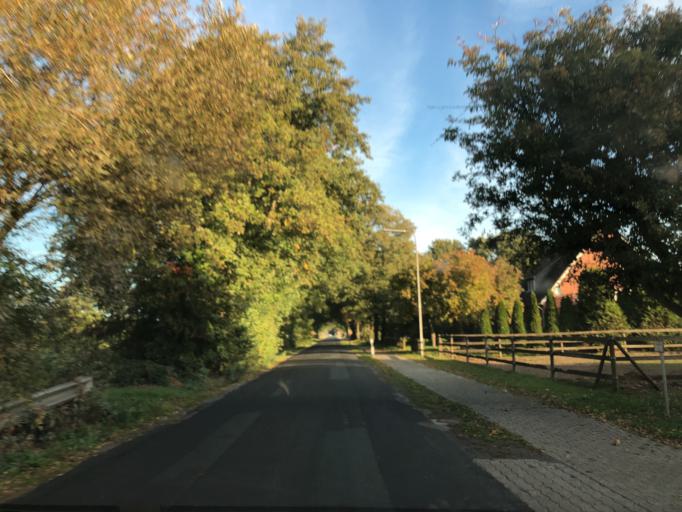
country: DE
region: Lower Saxony
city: Lehe
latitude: 53.0433
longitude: 7.3457
